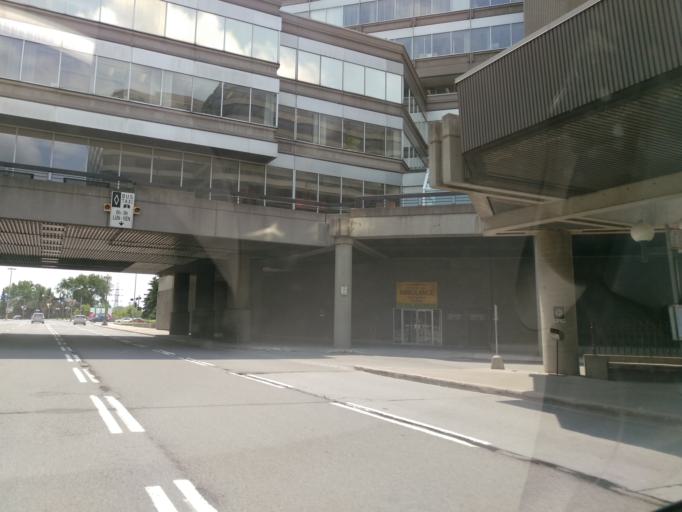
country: CA
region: Ontario
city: Ottawa
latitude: 45.4260
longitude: -75.7141
